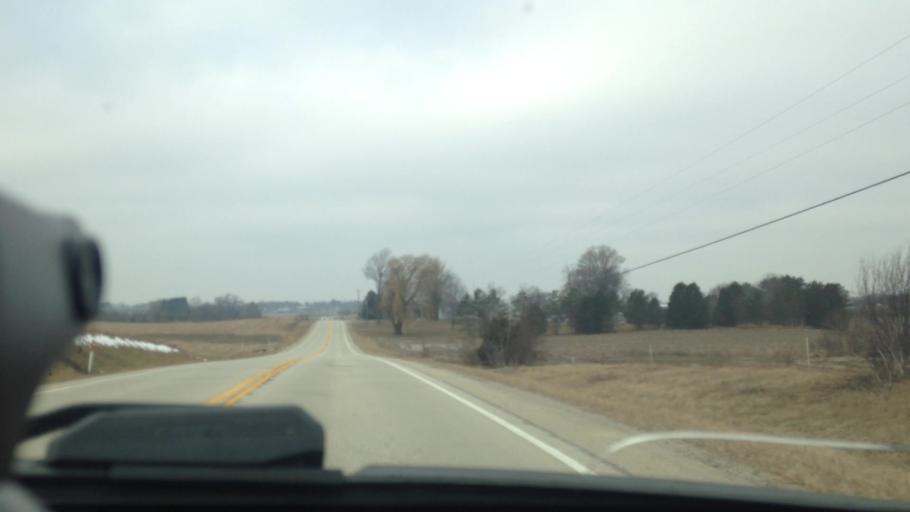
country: US
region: Wisconsin
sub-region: Dodge County
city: Beaver Dam
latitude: 43.4843
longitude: -88.7935
